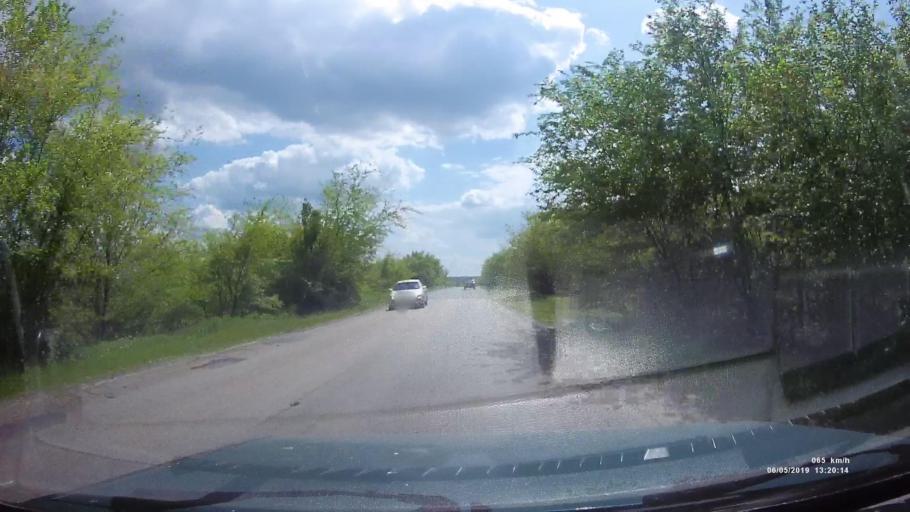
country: RU
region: Rostov
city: Ust'-Donetskiy
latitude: 47.7181
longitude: 40.9115
